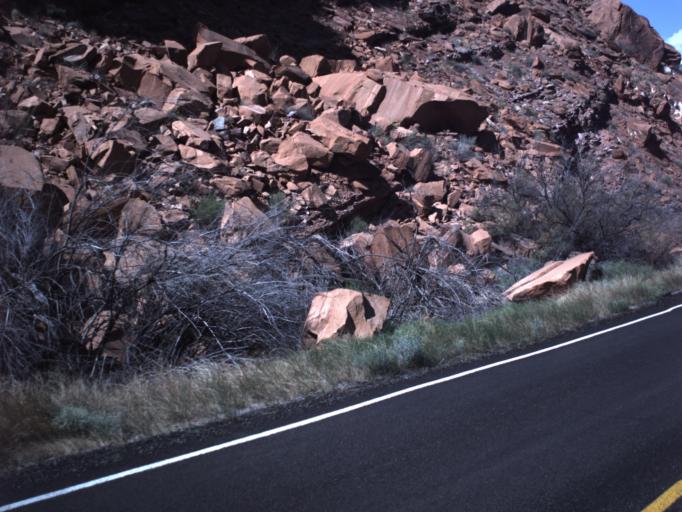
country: US
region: Utah
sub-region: Grand County
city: Moab
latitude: 38.5708
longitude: -109.5804
